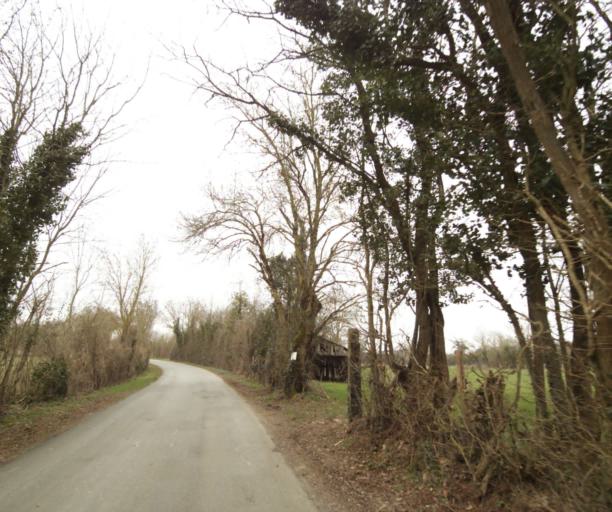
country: FR
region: Poitou-Charentes
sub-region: Departement des Deux-Sevres
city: Magne
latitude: 46.3275
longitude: -0.5283
